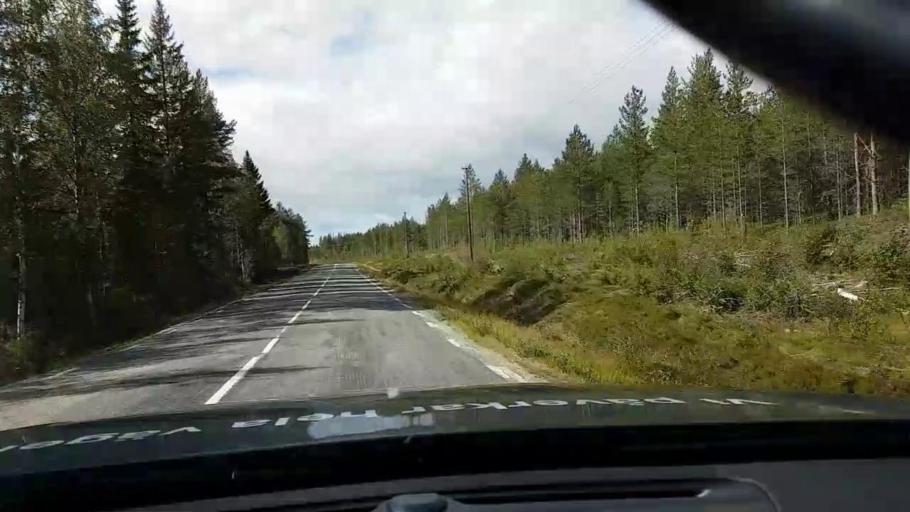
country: SE
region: Vaesterbotten
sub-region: Asele Kommun
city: Asele
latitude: 63.8469
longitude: 17.4141
